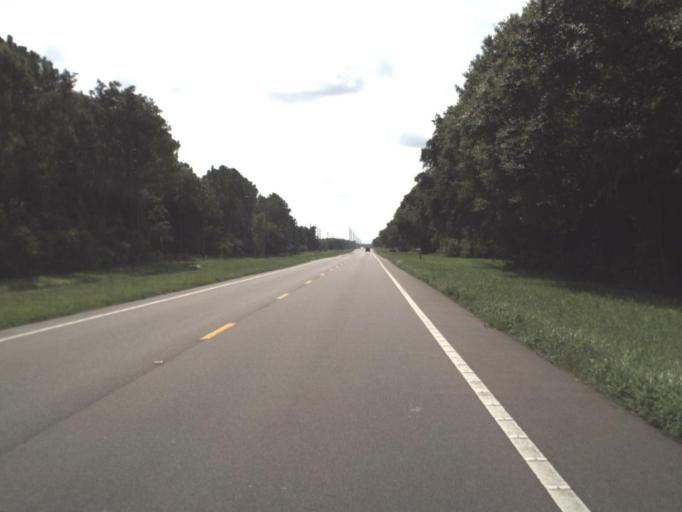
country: US
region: Florida
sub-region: Pasco County
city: Zephyrhills North
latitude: 28.2664
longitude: -82.0885
